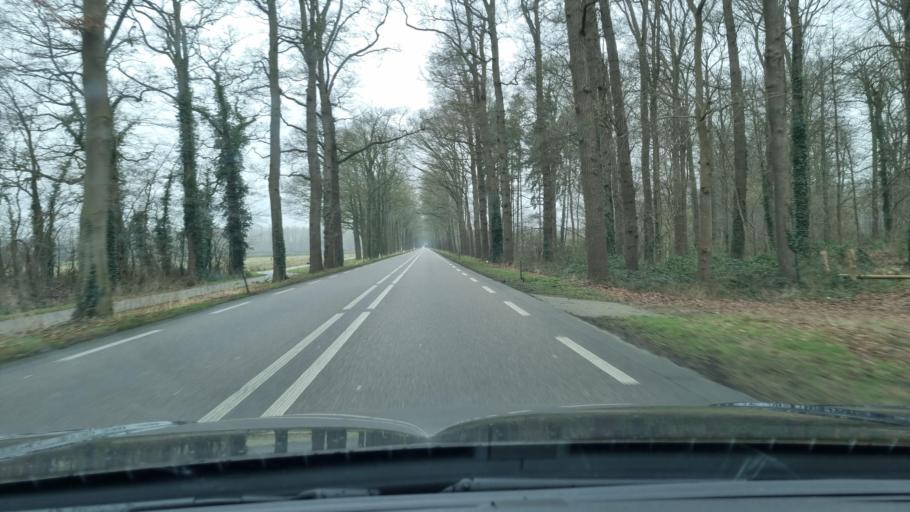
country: NL
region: Gelderland
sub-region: Gemeente Bronckhorst
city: Baak
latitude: 52.0150
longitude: 6.2266
